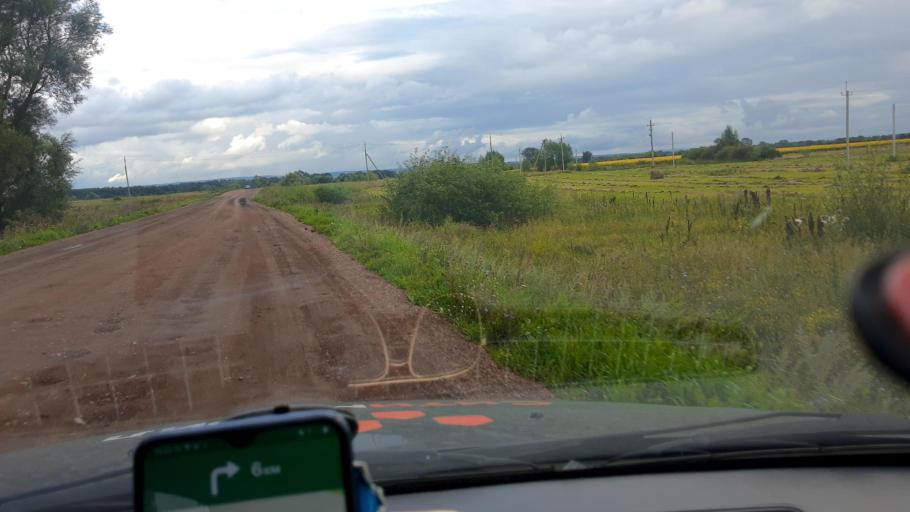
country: RU
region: Bashkortostan
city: Karmaskaly
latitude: 53.9896
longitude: 56.2928
